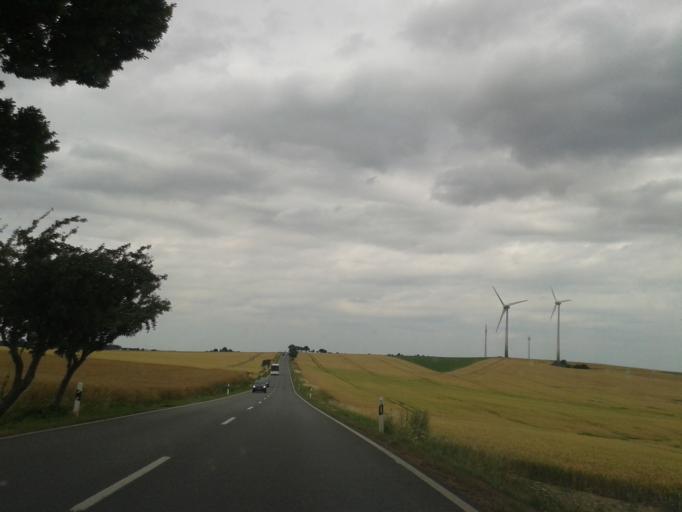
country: DE
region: Saxony
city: Niederschona
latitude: 50.9833
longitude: 13.4467
